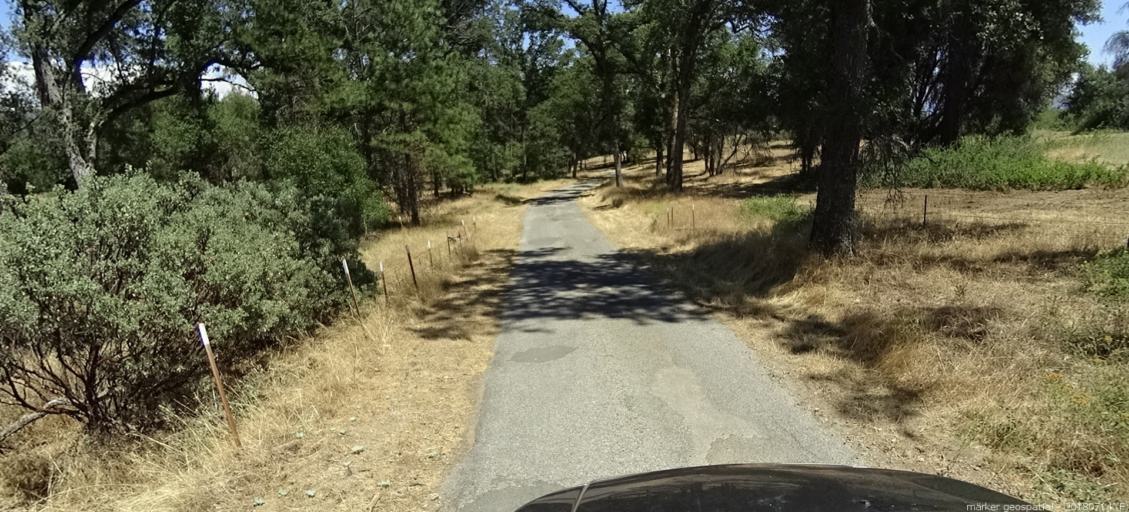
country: US
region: California
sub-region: Madera County
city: Ahwahnee
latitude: 37.3920
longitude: -119.7545
